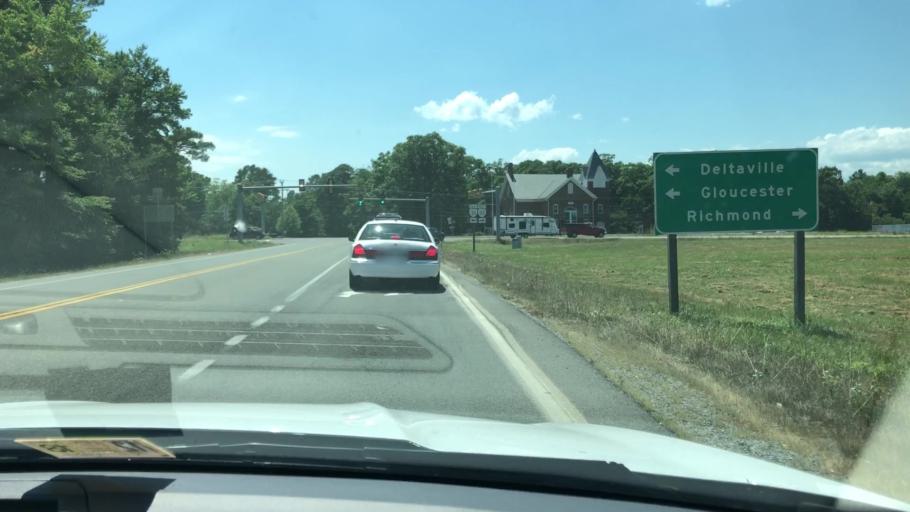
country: US
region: Virginia
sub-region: Middlesex County
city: Saluda
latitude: 37.5823
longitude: -76.4862
